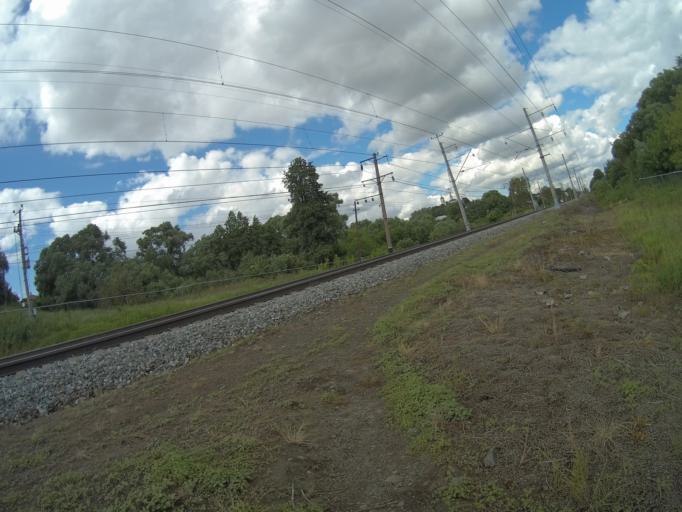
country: RU
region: Vladimir
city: Vladimir
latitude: 56.1169
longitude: 40.3932
